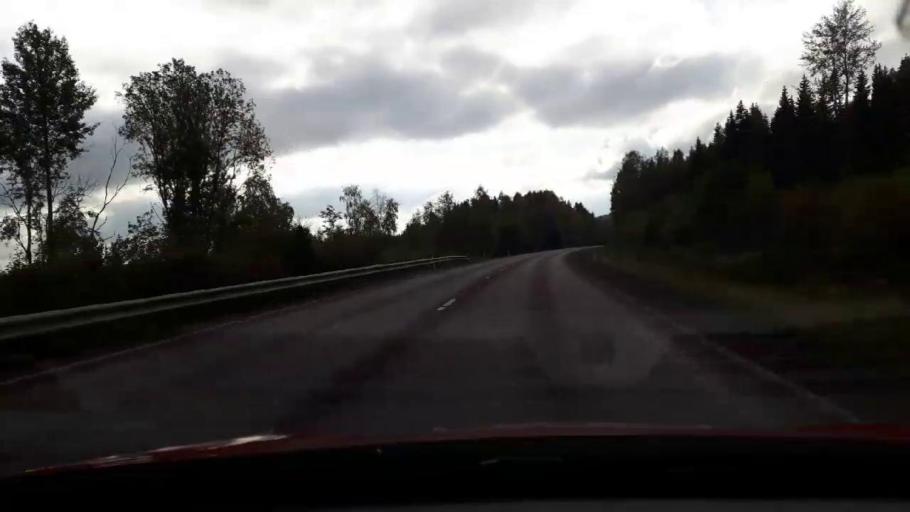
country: SE
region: Gaevleborg
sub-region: Ljusdals Kommun
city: Jaervsoe
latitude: 61.6149
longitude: 16.2951
